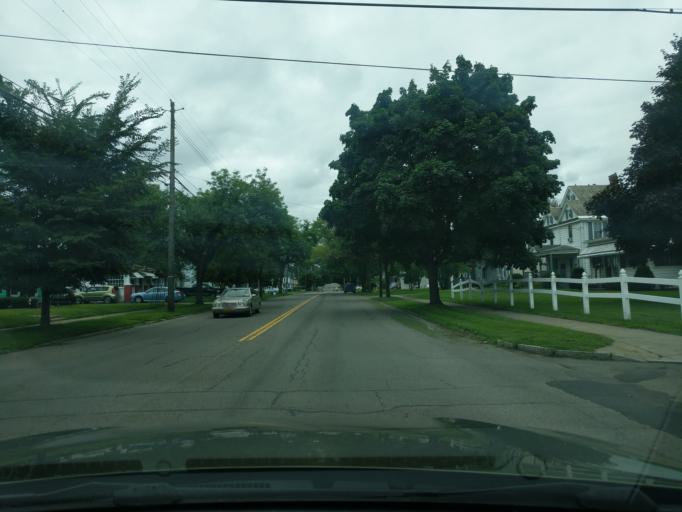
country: US
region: New York
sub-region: Chemung County
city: Elmira
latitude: 42.1075
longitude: -76.8192
